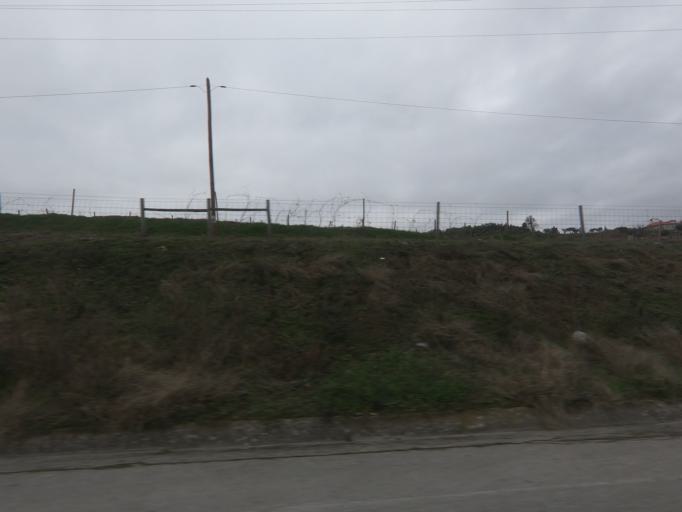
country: PT
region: Viseu
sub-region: Lamego
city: Lamego
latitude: 41.0840
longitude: -7.7915
